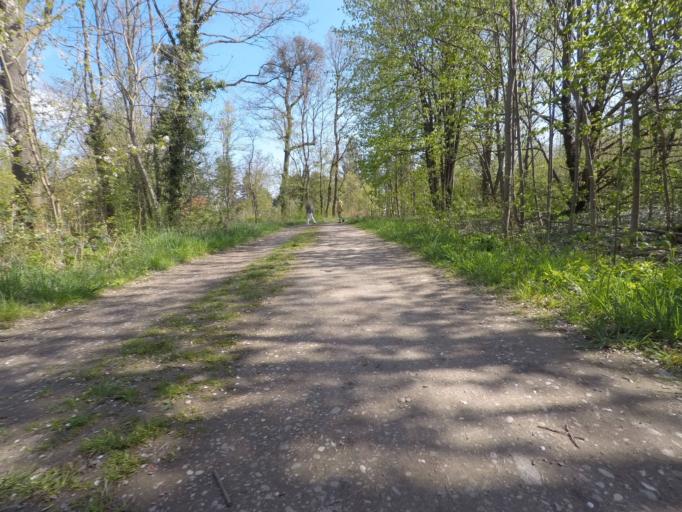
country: AT
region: Lower Austria
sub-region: Politischer Bezirk Modling
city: Perchtoldsdorf
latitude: 48.1719
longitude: 16.2597
